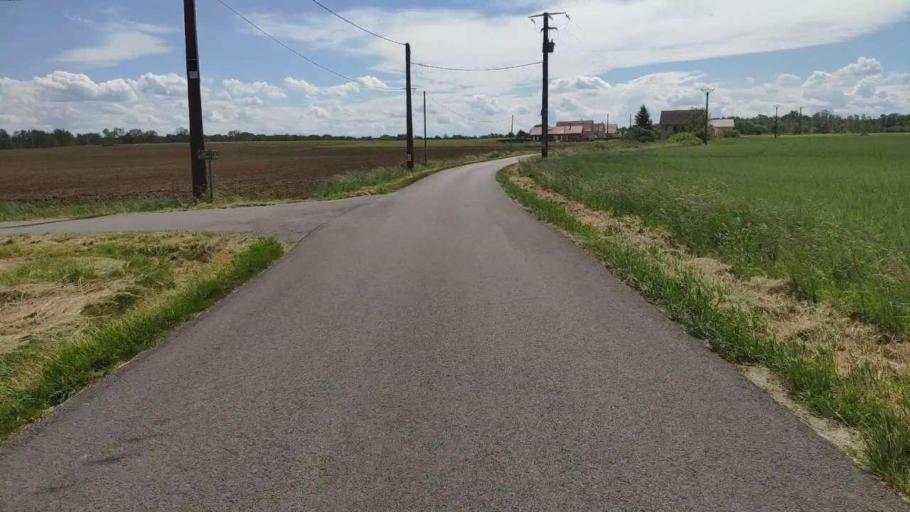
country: FR
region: Franche-Comte
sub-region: Departement du Jura
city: Bletterans
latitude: 46.7086
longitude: 5.4196
